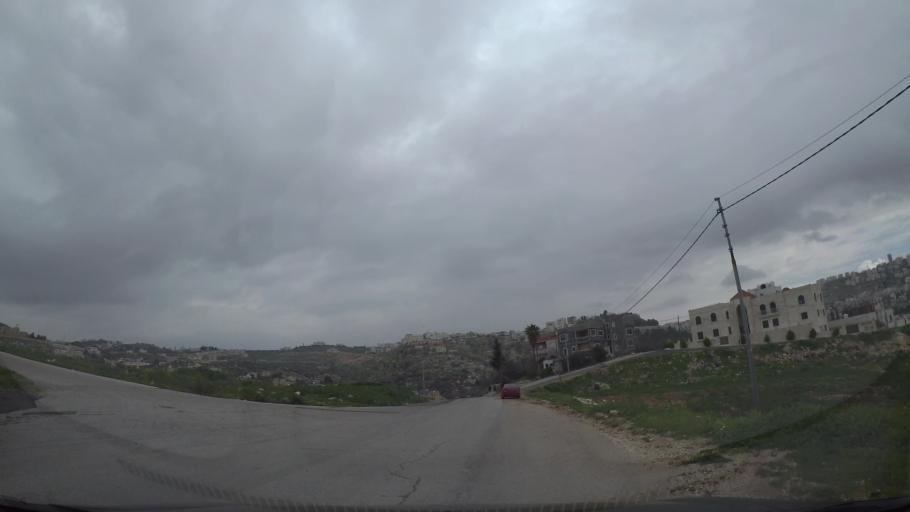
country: JO
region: Amman
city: Wadi as Sir
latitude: 31.9572
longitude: 35.8110
